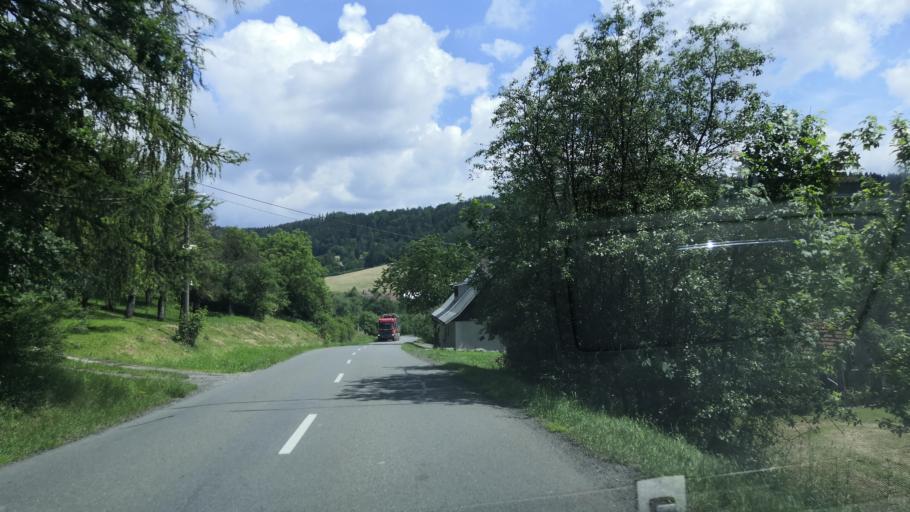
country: CZ
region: Zlin
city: Valasska Bystrice
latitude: 49.4257
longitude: 18.1177
